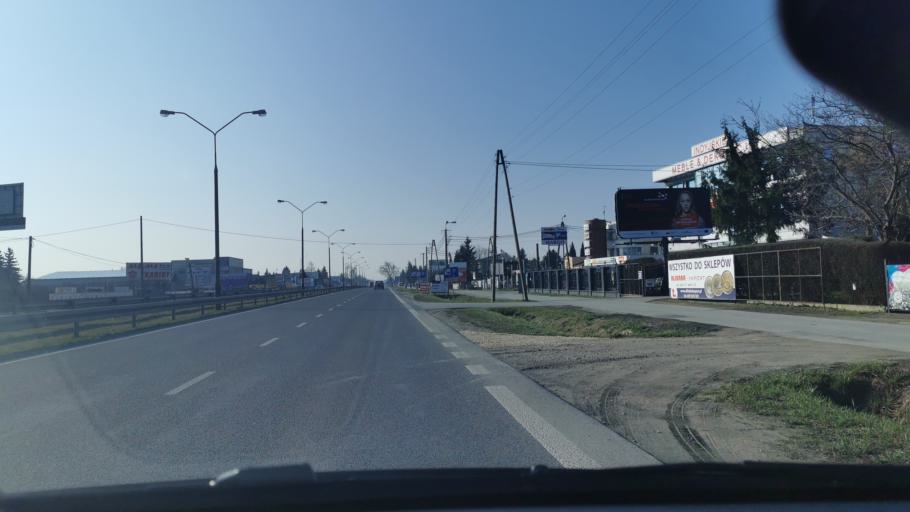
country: PL
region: Masovian Voivodeship
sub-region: Powiat pruszkowski
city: Nowe Grocholice
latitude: 52.1285
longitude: 20.8964
